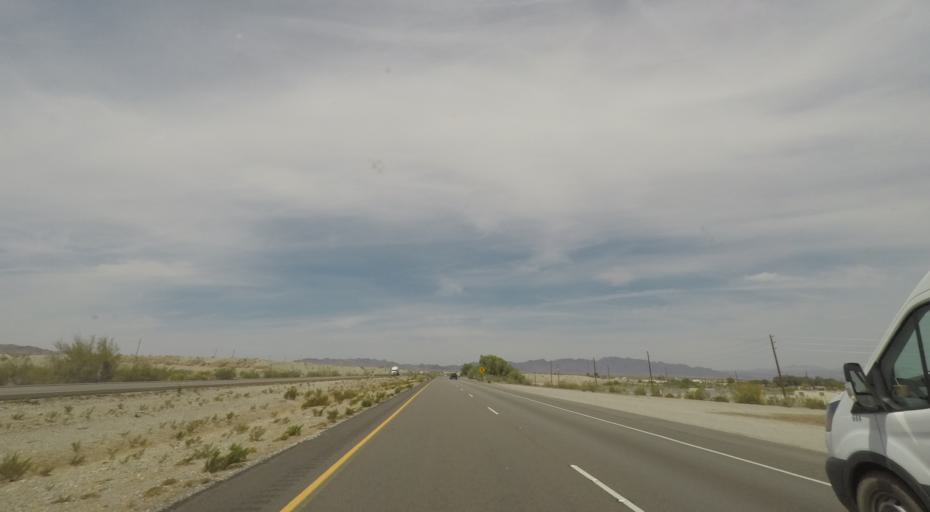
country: US
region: California
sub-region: San Bernardino County
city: Needles
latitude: 34.8551
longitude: -114.6280
